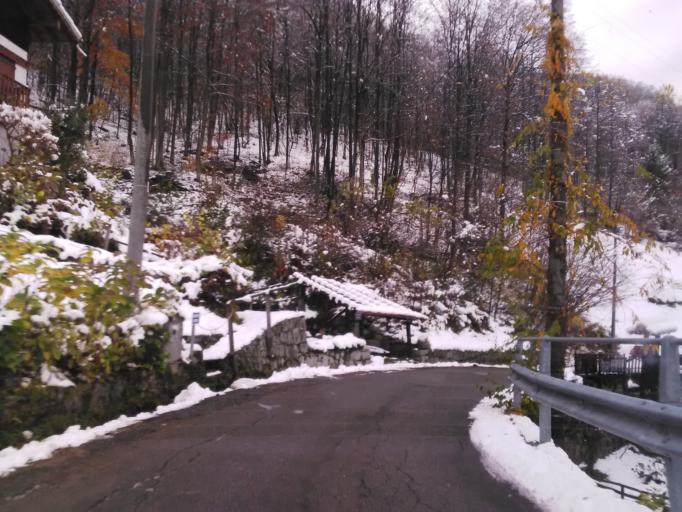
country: IT
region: Piedmont
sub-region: Provincia di Vercelli
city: Varallo
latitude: 45.7991
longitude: 8.2552
